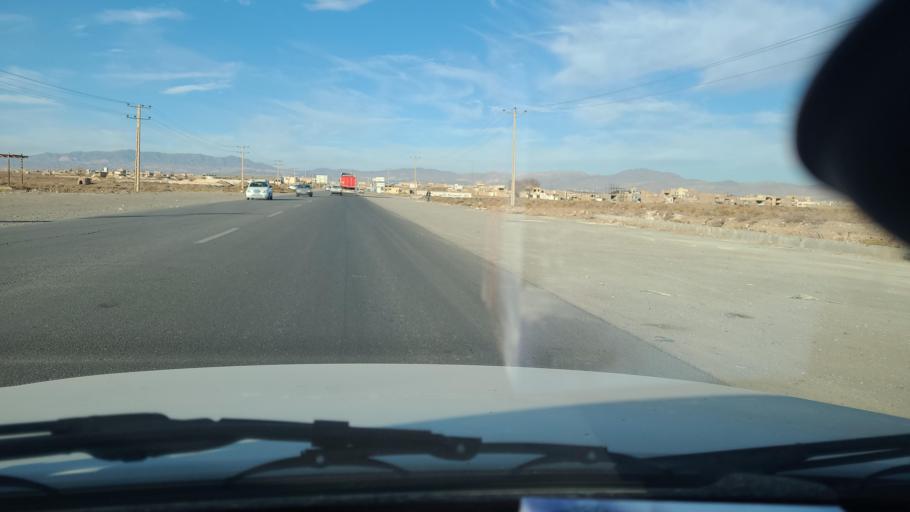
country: IR
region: Razavi Khorasan
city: Sabzevar
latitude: 36.2089
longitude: 57.6504
